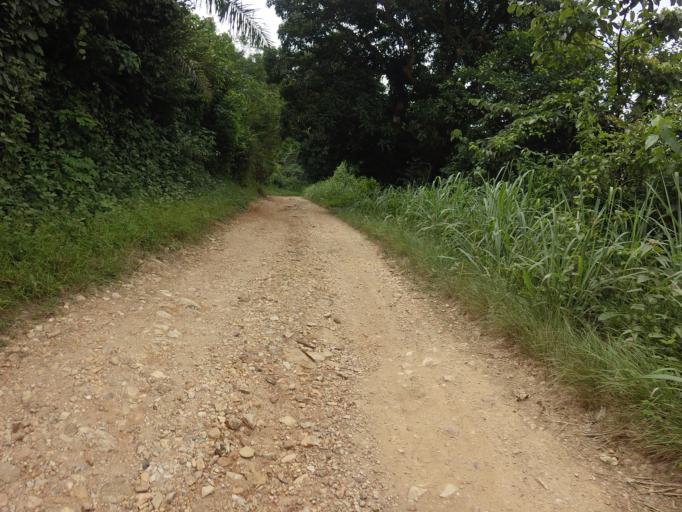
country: GH
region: Volta
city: Kpandu
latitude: 6.8699
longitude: 0.4411
